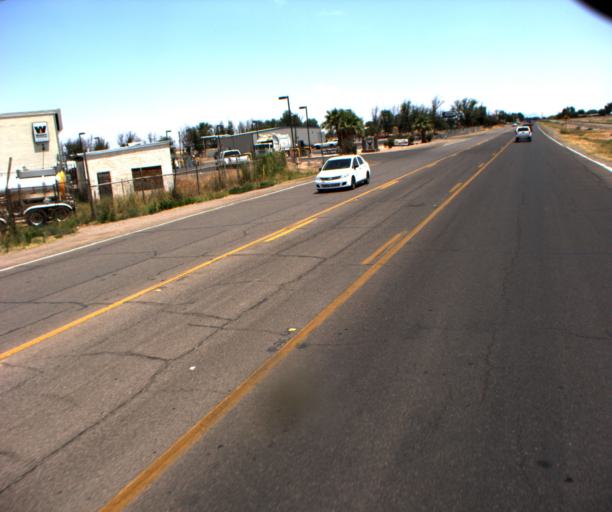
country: US
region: Arizona
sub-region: Graham County
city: Safford
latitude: 32.8302
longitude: -109.6972
